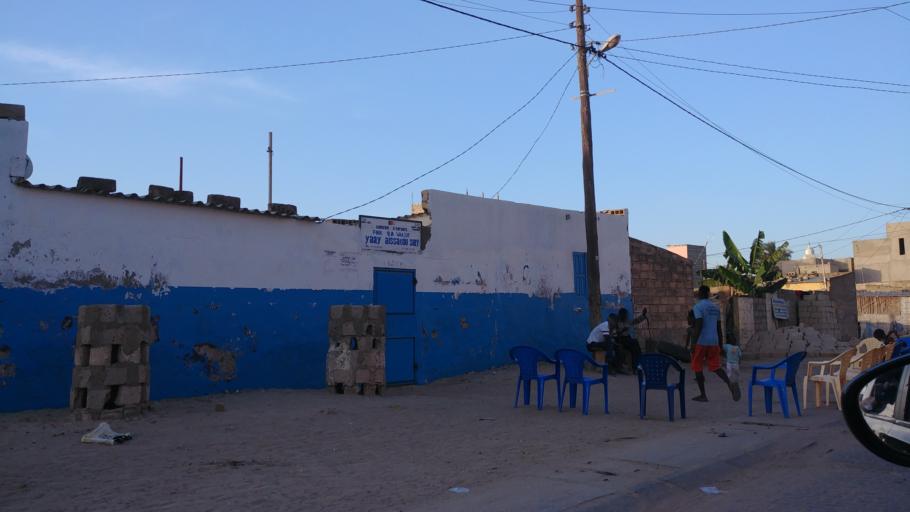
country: SN
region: Saint-Louis
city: Saint-Louis
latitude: 16.0209
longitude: -16.4966
